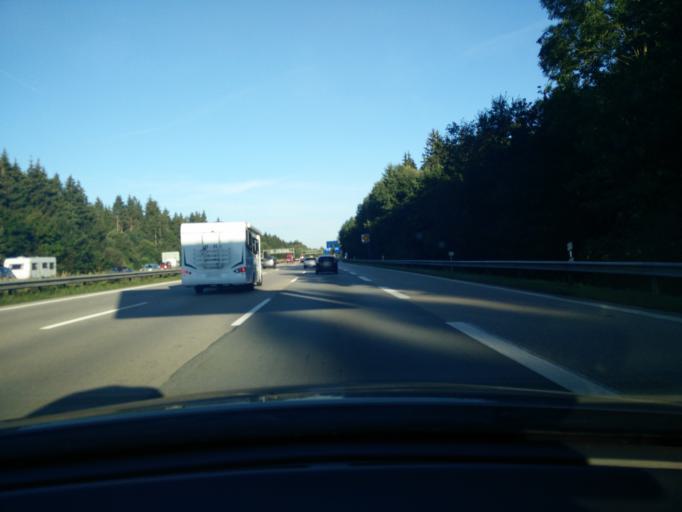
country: DE
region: Bavaria
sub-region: Upper Bavaria
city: Holzkirchen
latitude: 47.8888
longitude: 11.7378
